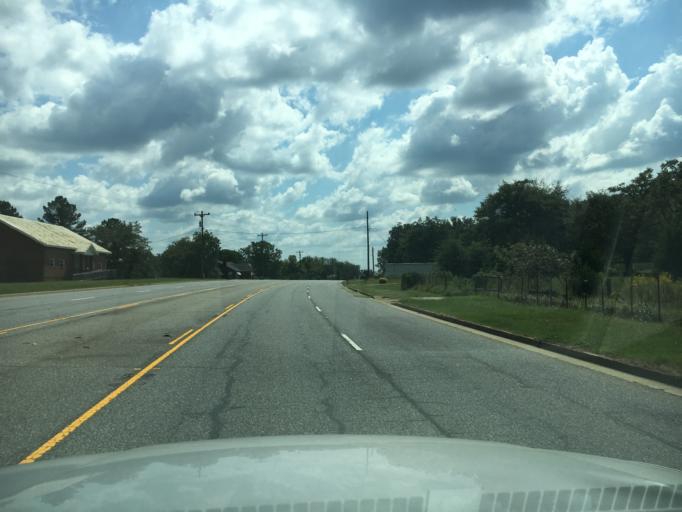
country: US
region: South Carolina
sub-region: Greenwood County
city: Ware Shoals
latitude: 34.4991
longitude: -82.2883
